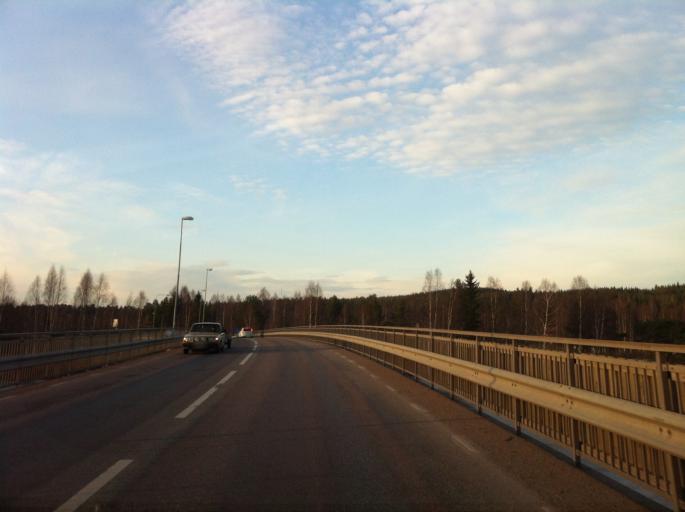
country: SE
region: Dalarna
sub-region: Vansbro Kommun
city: Vansbro
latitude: 60.5089
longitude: 14.2393
